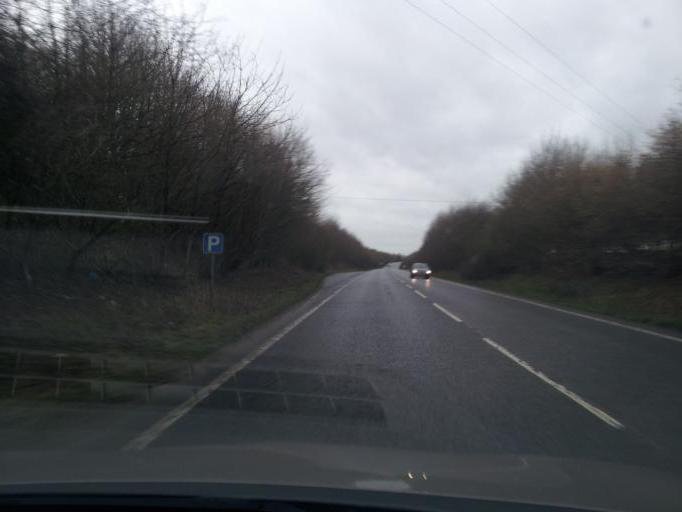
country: GB
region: England
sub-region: Norfolk
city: Diss
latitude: 52.3616
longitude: 1.1206
